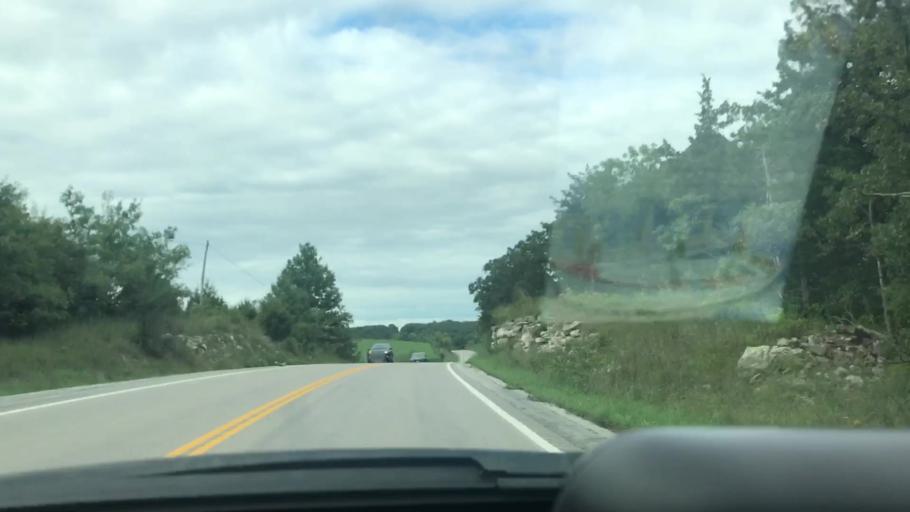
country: US
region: Missouri
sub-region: Benton County
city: Warsaw
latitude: 38.1270
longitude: -93.2805
